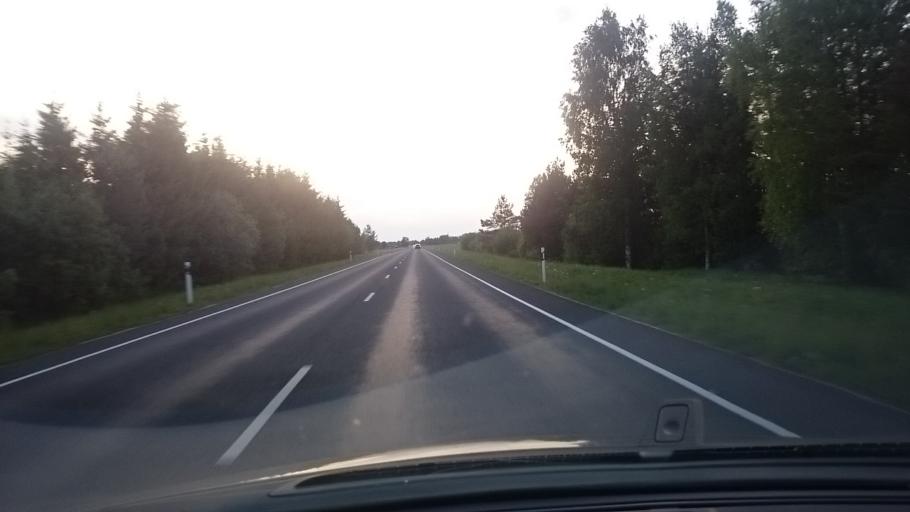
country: EE
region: Viljandimaa
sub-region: Vohma linn
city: Vohma
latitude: 58.7442
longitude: 25.5772
